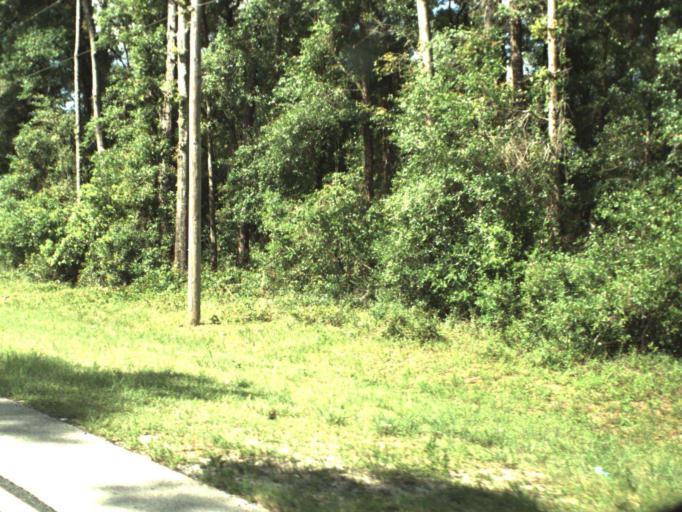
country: US
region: Florida
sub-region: Marion County
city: Belleview
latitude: 29.1007
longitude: -82.0878
